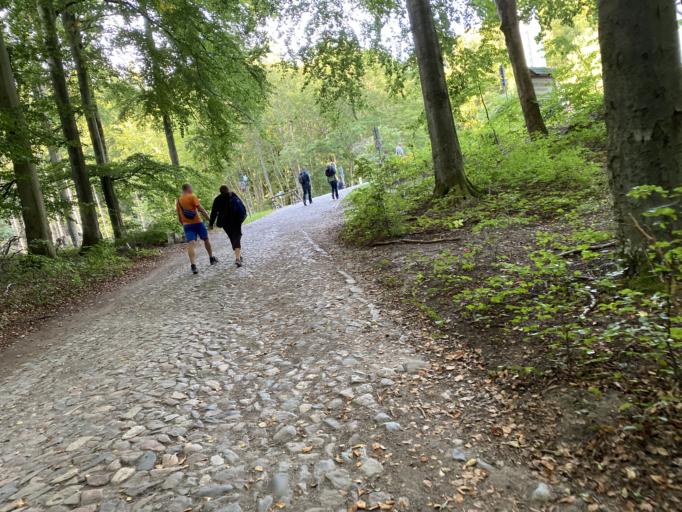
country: DE
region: Mecklenburg-Vorpommern
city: Sassnitz
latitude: 54.5712
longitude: 13.6587
